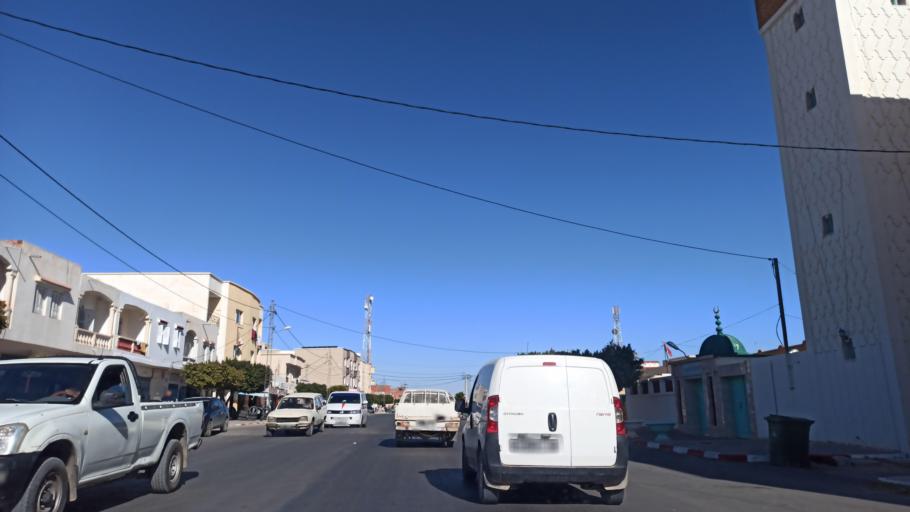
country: TN
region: Sidi Bu Zayd
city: Bi'r al Hufayy
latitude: 34.9255
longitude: 9.1908
